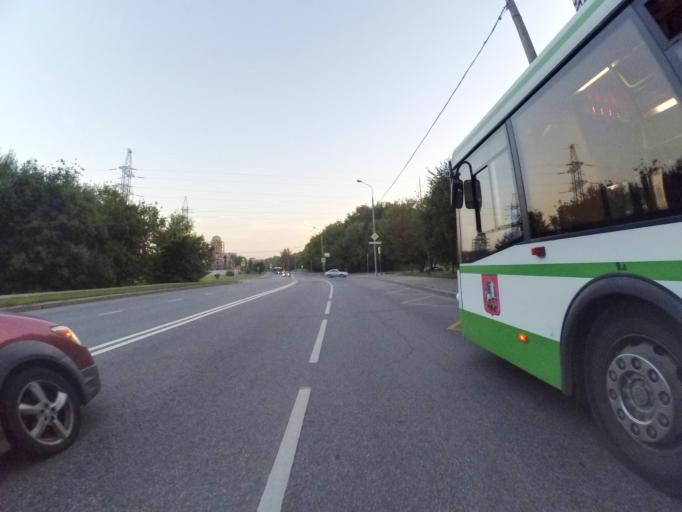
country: RU
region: Moscow
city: Strogino
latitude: 55.8374
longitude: 37.4061
